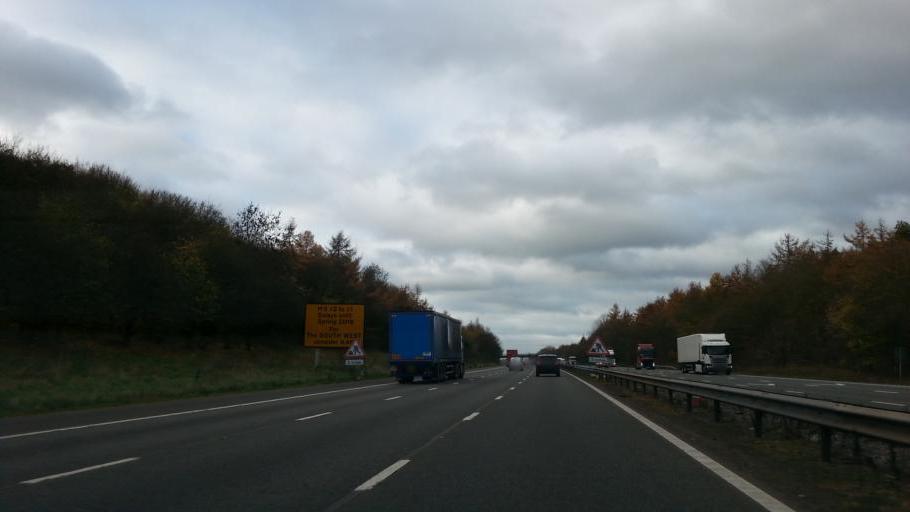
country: GB
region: England
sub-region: Warwickshire
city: Long Lawford
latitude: 52.4320
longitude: -1.3345
